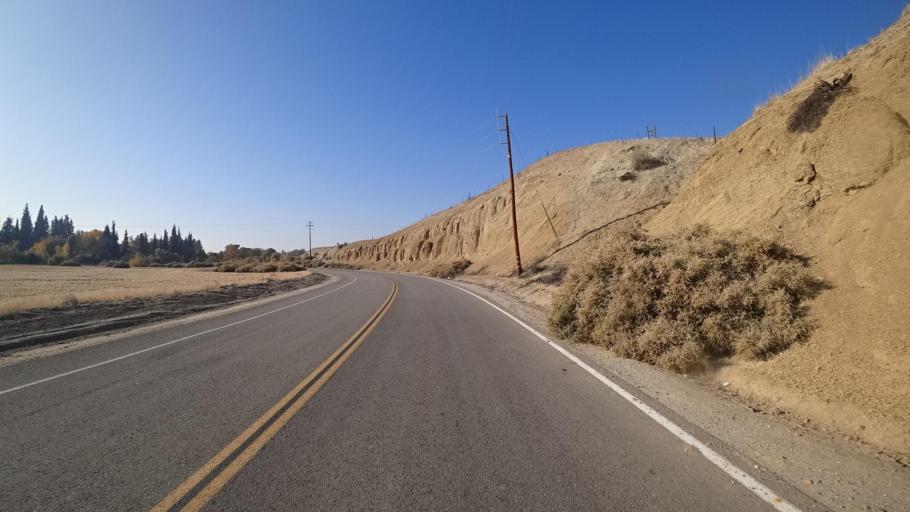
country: US
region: California
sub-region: Kern County
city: Oildale
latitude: 35.4507
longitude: -118.9029
